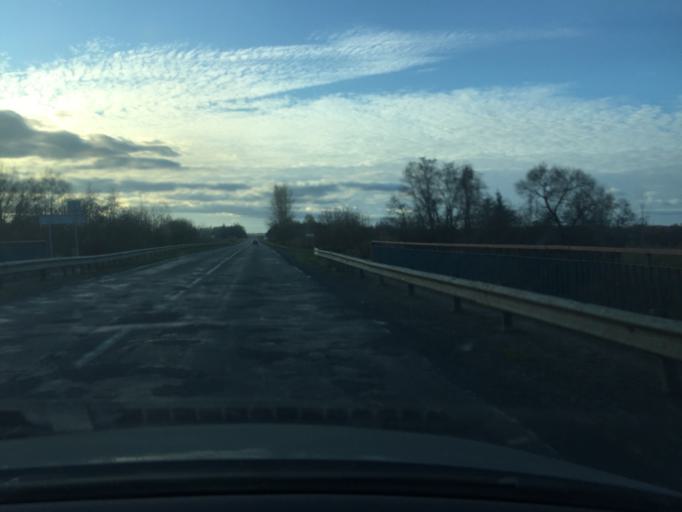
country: BY
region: Vitebsk
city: Vyerkhnyadzvinsk
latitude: 55.8382
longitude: 27.8832
